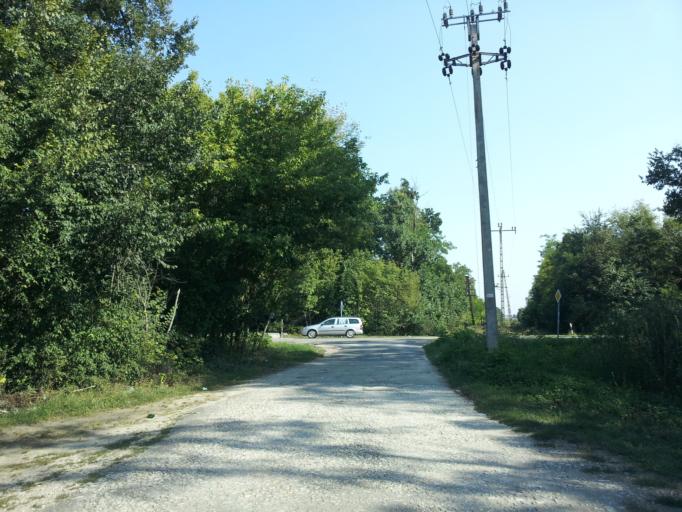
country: HU
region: Fejer
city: Polgardi
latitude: 47.0234
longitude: 18.2825
